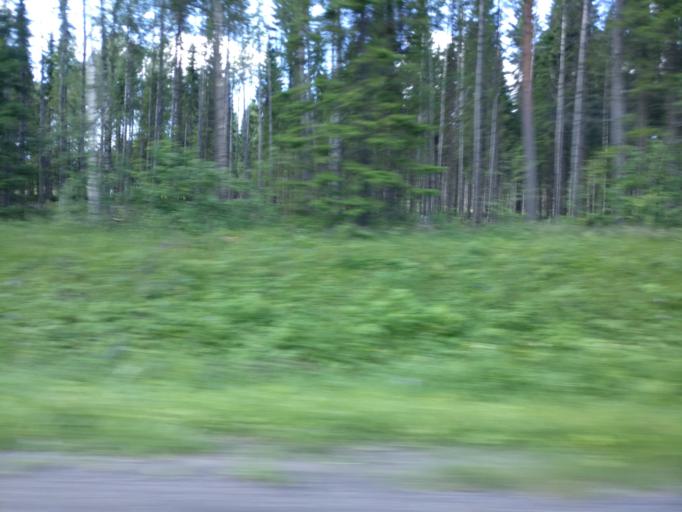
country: FI
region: Southern Savonia
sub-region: Savonlinna
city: Kerimaeki
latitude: 61.8794
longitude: 29.1111
